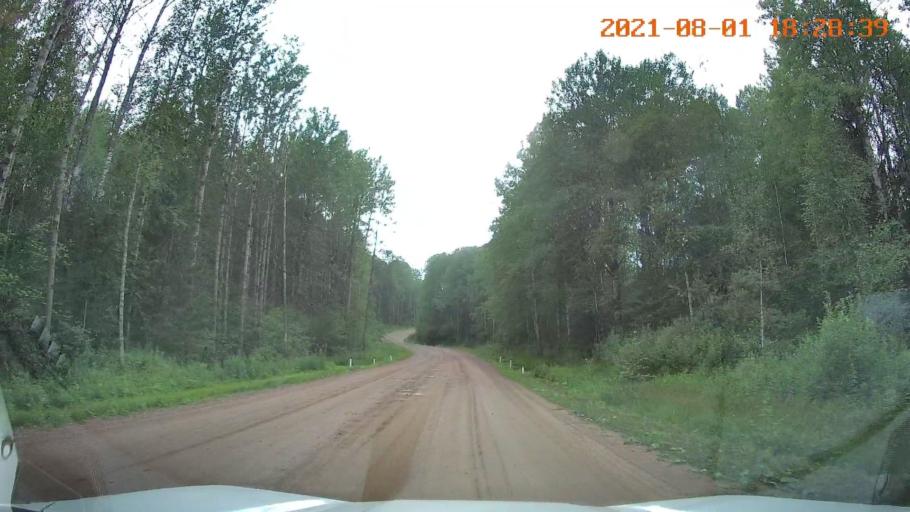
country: RU
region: Leningrad
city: Voznesen'ye
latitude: 60.8848
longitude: 35.3896
